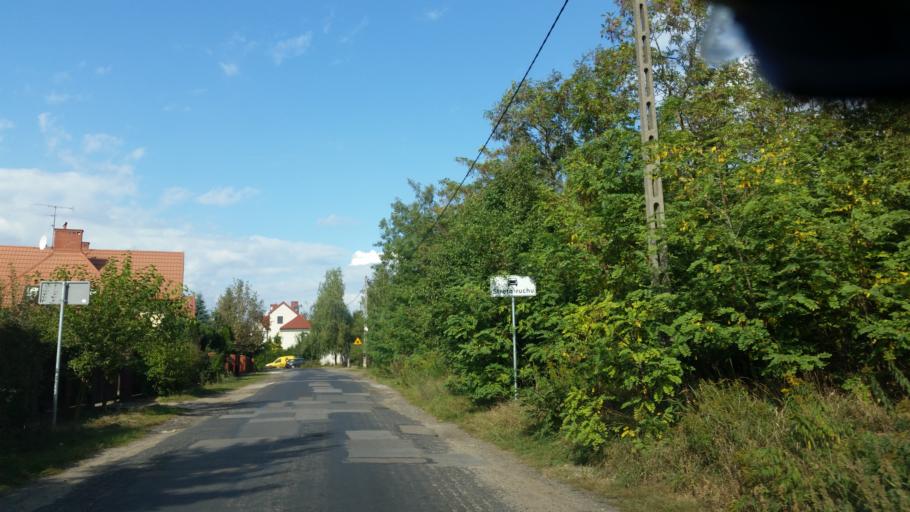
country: PL
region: Masovian Voivodeship
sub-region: Warszawa
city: Targowek
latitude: 52.3154
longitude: 21.0434
